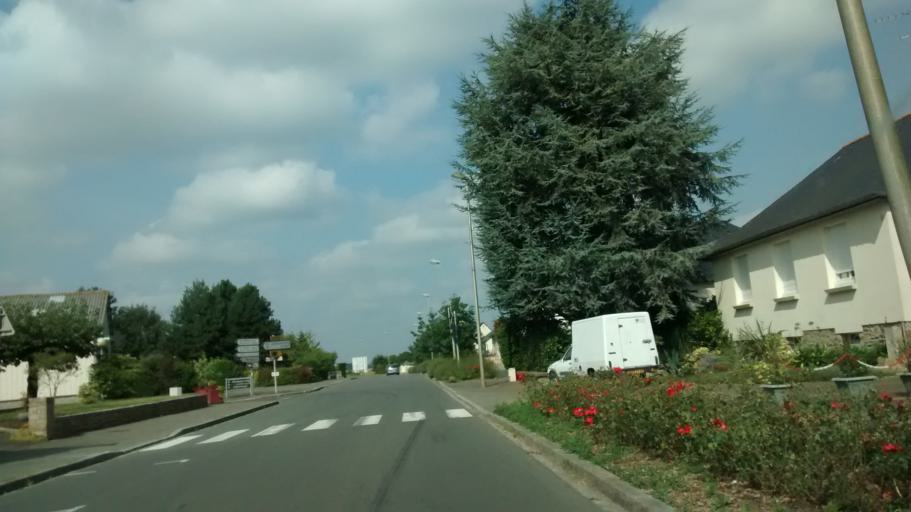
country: FR
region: Brittany
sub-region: Departement d'Ille-et-Vilaine
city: Livre-sur-Changeon
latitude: 48.2211
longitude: -1.3460
